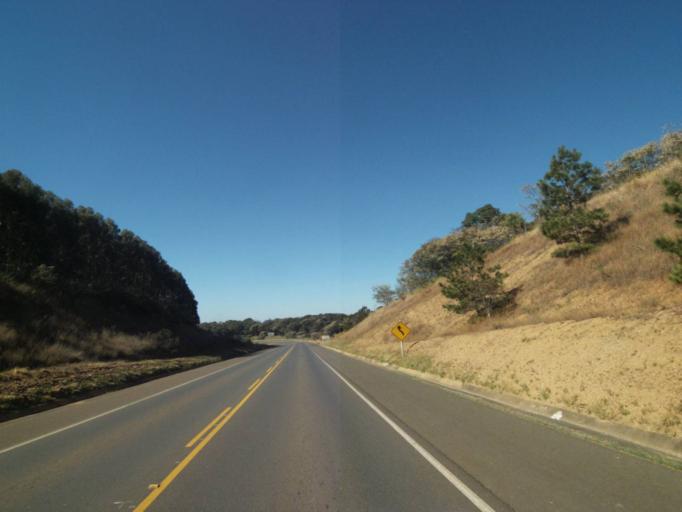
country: BR
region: Parana
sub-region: Tibagi
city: Tibagi
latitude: -24.4073
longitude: -50.3478
